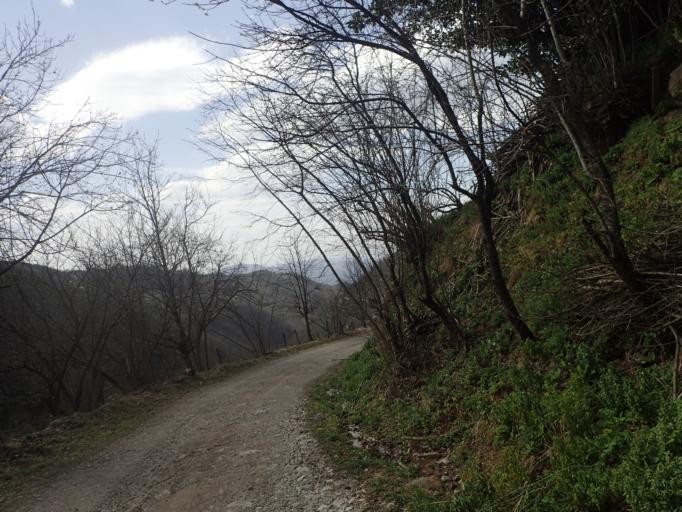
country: TR
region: Ordu
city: Kabaduz
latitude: 40.8143
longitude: 37.9016
